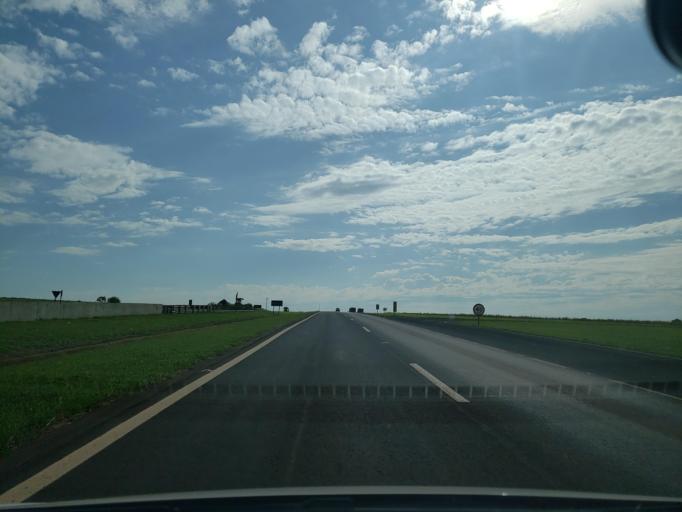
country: BR
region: Sao Paulo
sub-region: Promissao
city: Promissao
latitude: -21.5992
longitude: -49.8859
